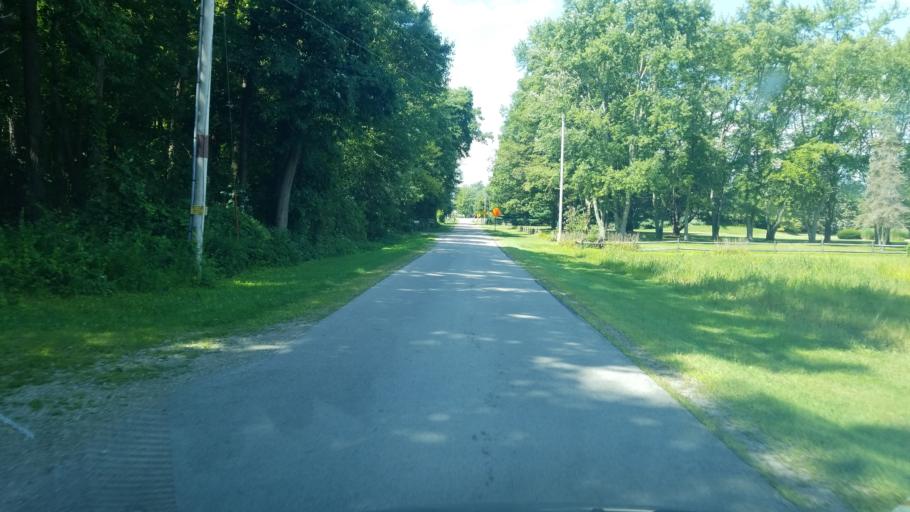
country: US
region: Ohio
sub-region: Lucas County
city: Whitehouse
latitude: 41.4315
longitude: -83.8685
